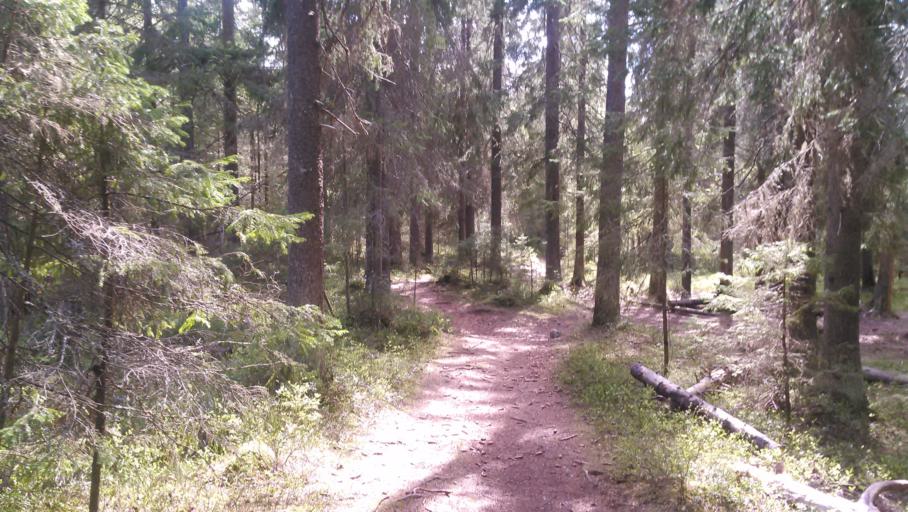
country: SE
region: Vaesterbotten
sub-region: Umea Kommun
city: Umea
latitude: 63.8388
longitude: 20.3030
